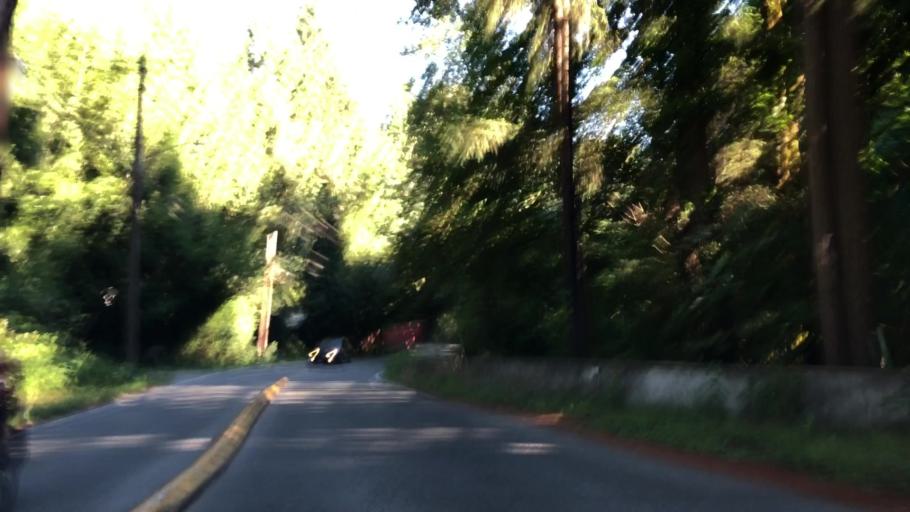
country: US
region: Washington
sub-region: Snohomish County
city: Martha Lake
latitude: 47.8285
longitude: -122.2534
